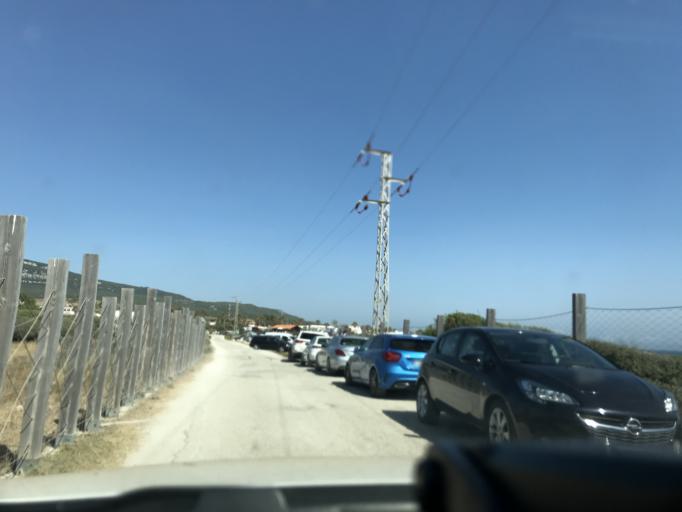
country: ES
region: Andalusia
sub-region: Provincia de Cadiz
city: Zahara de los Atunes
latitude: 36.0878
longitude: -5.7708
